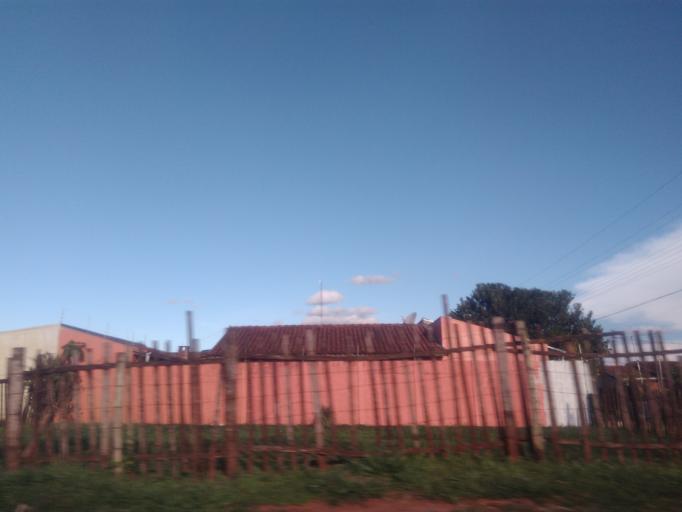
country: BR
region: Mato Grosso do Sul
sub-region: Ponta Pora
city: Ponta Pora
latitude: -22.5106
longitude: -55.7287
